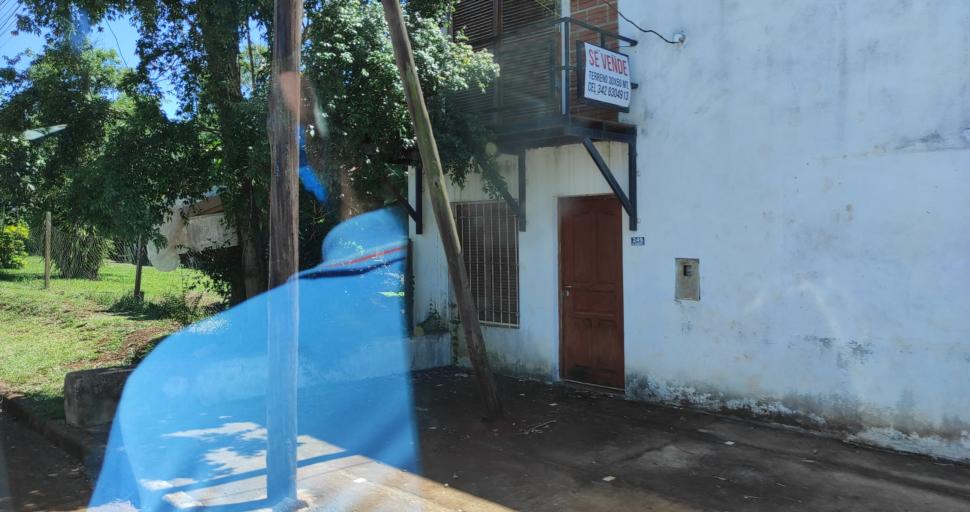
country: AR
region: Misiones
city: El Soberbio
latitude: -27.2996
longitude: -54.1940
